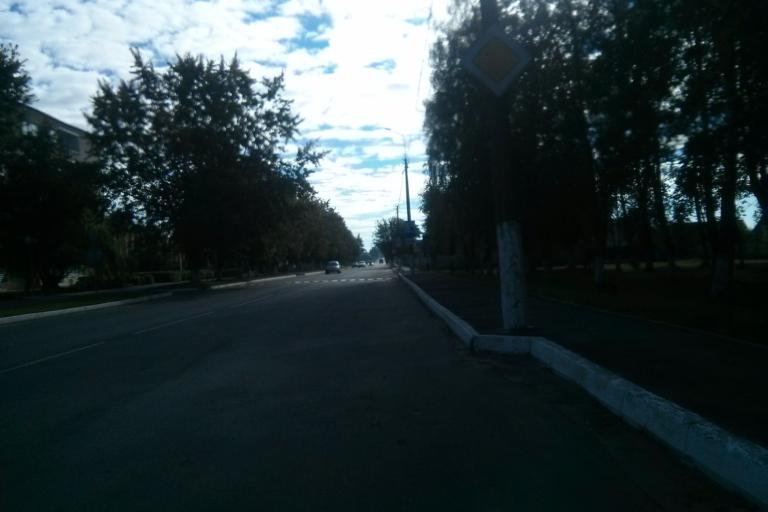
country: BY
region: Minsk
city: Chervyen'
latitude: 53.7183
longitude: 28.4028
